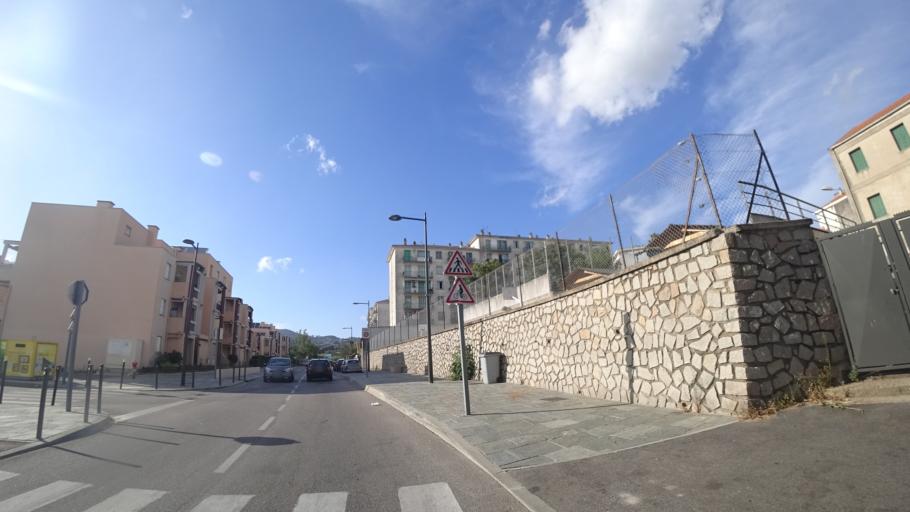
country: FR
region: Corsica
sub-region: Departement de la Corse-du-Sud
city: Ajaccio
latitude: 41.9349
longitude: 8.7436
